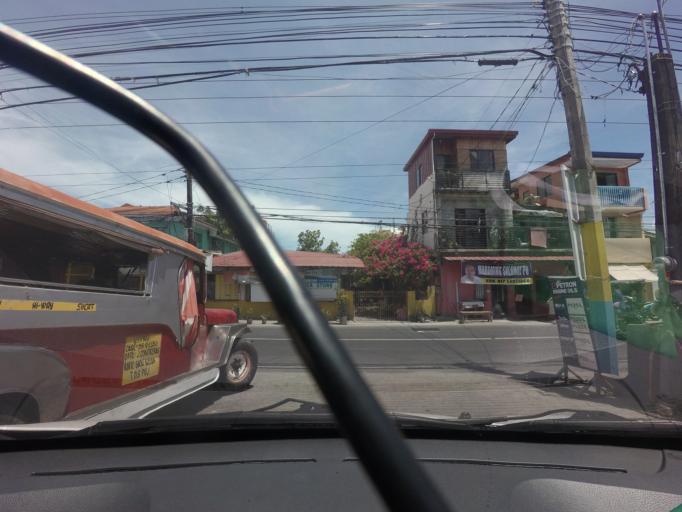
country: PH
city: Sambayanihan People's Village
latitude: 14.4631
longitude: 121.0551
